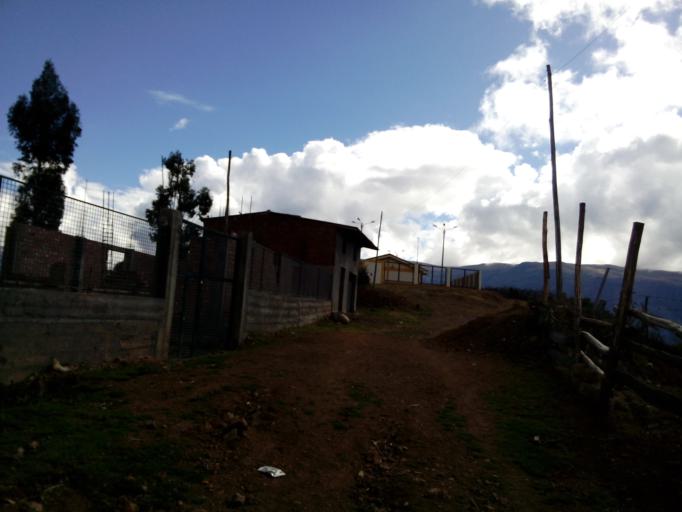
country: PE
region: Ayacucho
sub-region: Provincia de Victor Fajardo
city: Canaria
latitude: -13.8797
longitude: -73.9300
